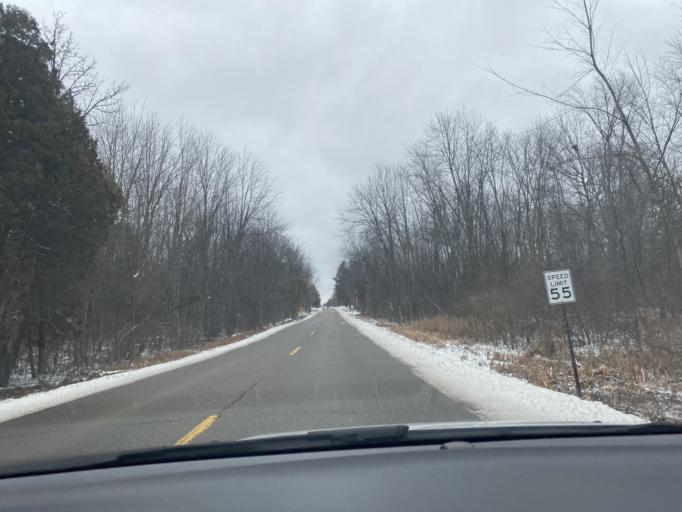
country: US
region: Michigan
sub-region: Lapeer County
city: Barnes Lake-Millers Lake
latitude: 43.2050
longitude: -83.2961
